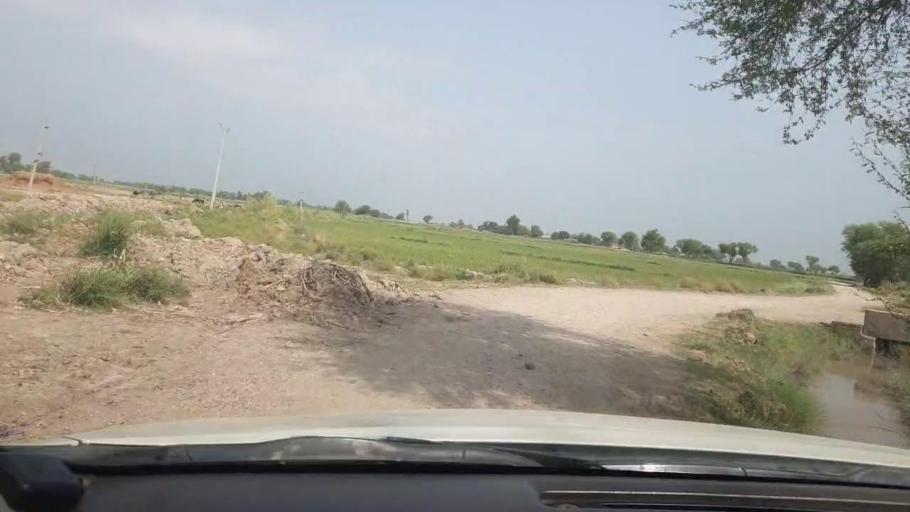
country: PK
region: Sindh
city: Shikarpur
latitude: 28.0162
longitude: 68.5937
